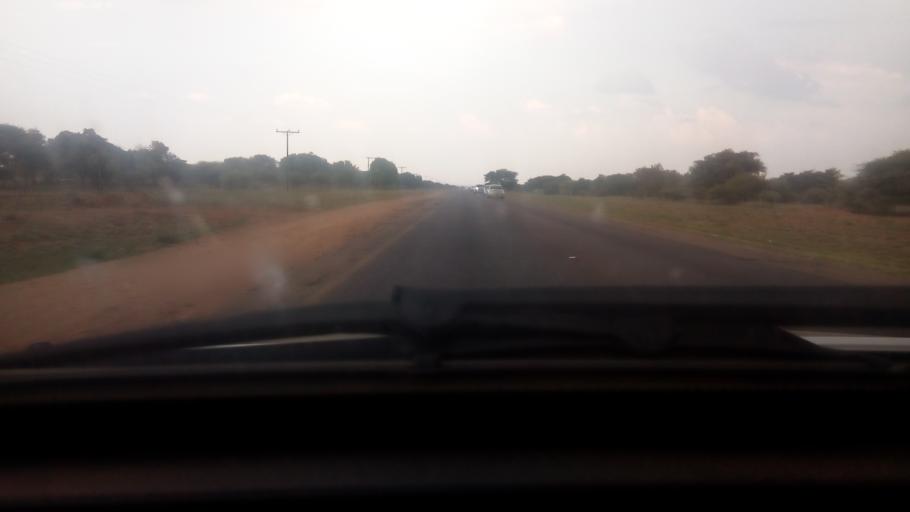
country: BW
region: Kweneng
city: Metsemotlhaba
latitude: -24.4871
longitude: 25.7384
